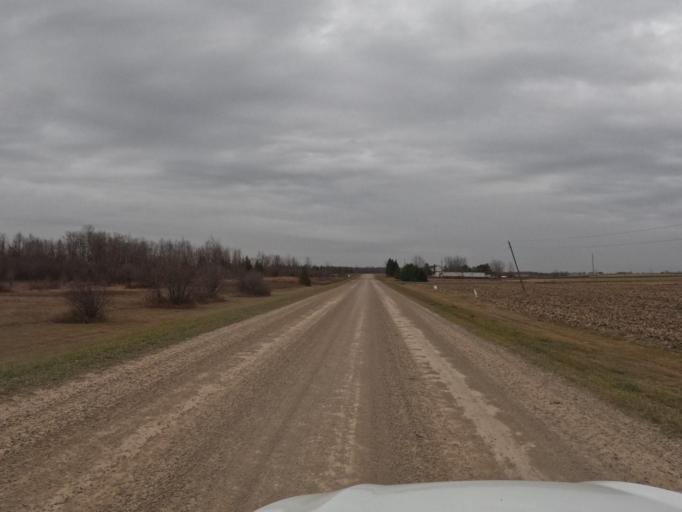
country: CA
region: Ontario
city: Shelburne
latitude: 43.8743
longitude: -80.3565
